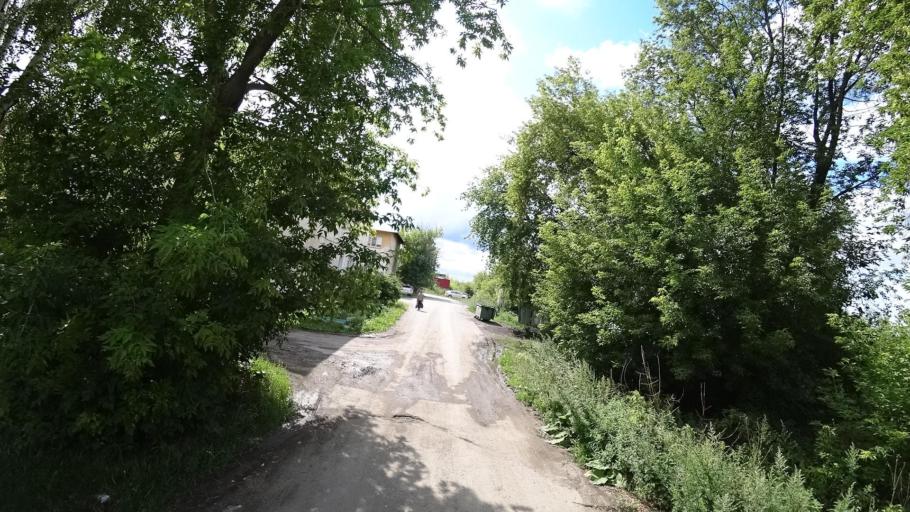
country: RU
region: Sverdlovsk
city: Kamyshlov
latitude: 56.8547
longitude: 62.7140
